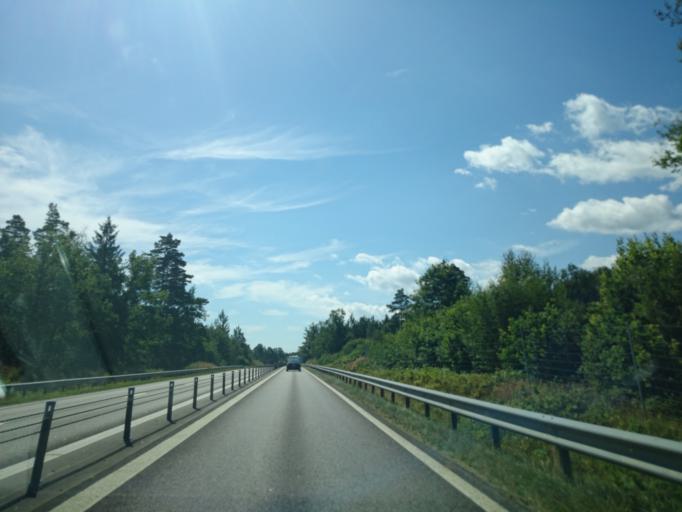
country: SE
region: Kalmar
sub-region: Monsteras Kommun
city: Timmernabben
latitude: 56.8579
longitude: 16.3787
